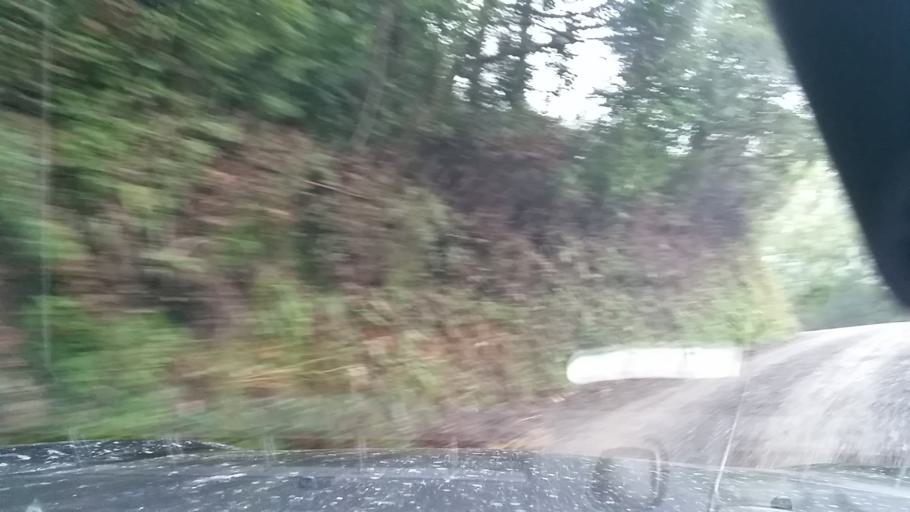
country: NZ
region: Nelson
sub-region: Nelson City
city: Nelson
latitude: -41.3624
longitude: 173.6099
